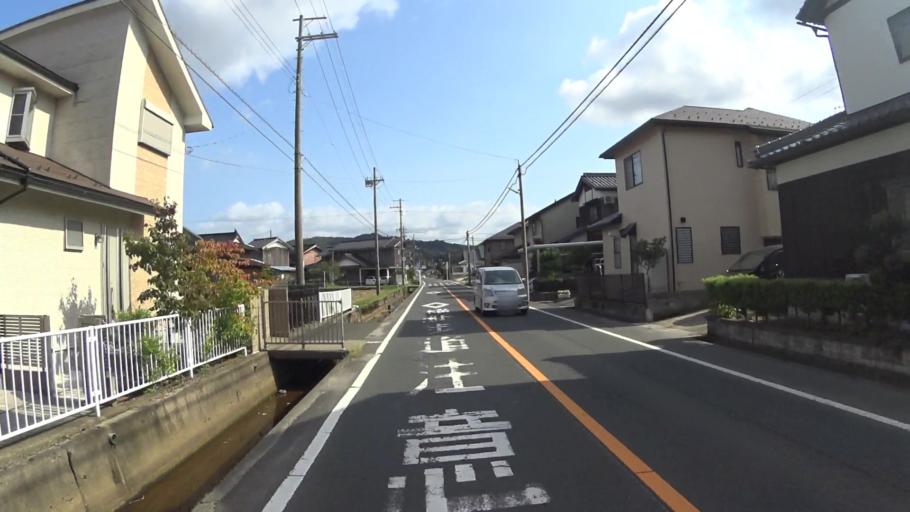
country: JP
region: Kyoto
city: Miyazu
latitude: 35.5926
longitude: 135.0987
